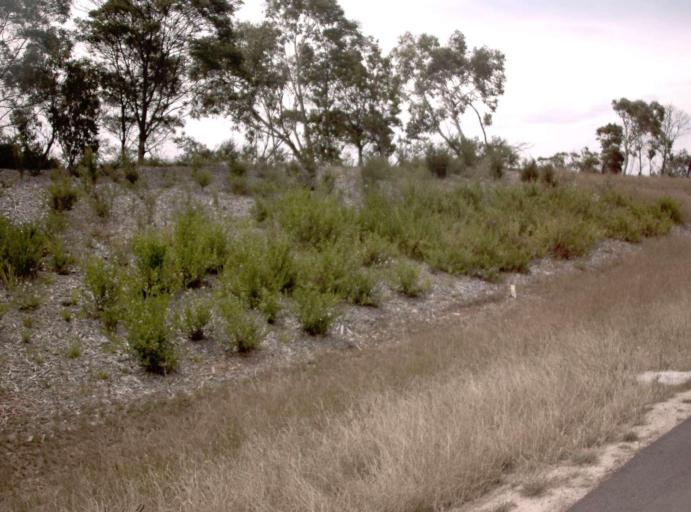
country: AU
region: Victoria
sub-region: Mornington Peninsula
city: Mount Martha
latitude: -38.2688
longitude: 145.0709
